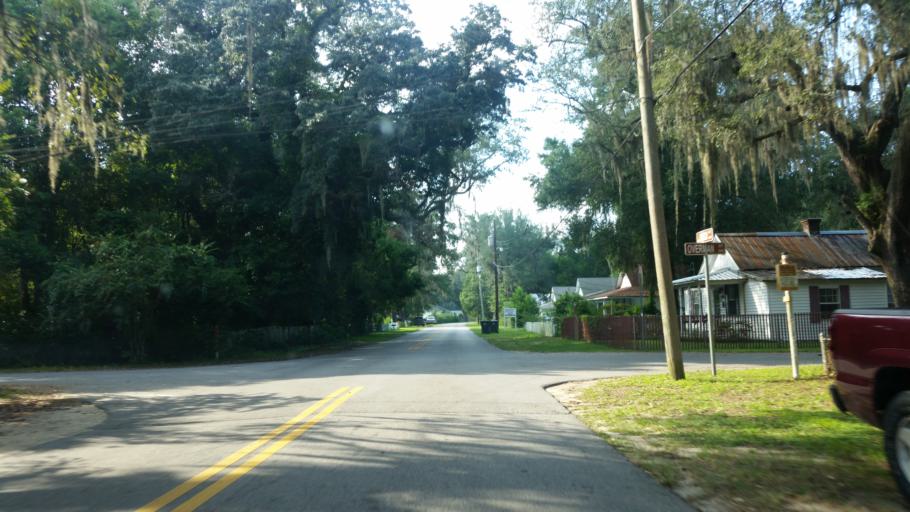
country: US
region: Florida
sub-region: Santa Rosa County
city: Bagdad
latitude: 30.5990
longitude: -87.0326
